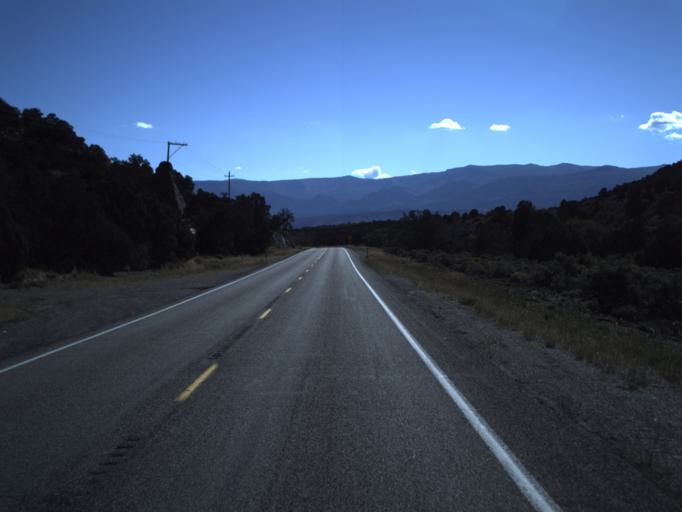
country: US
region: Utah
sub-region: Iron County
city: Cedar City
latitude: 37.6362
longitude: -113.2772
